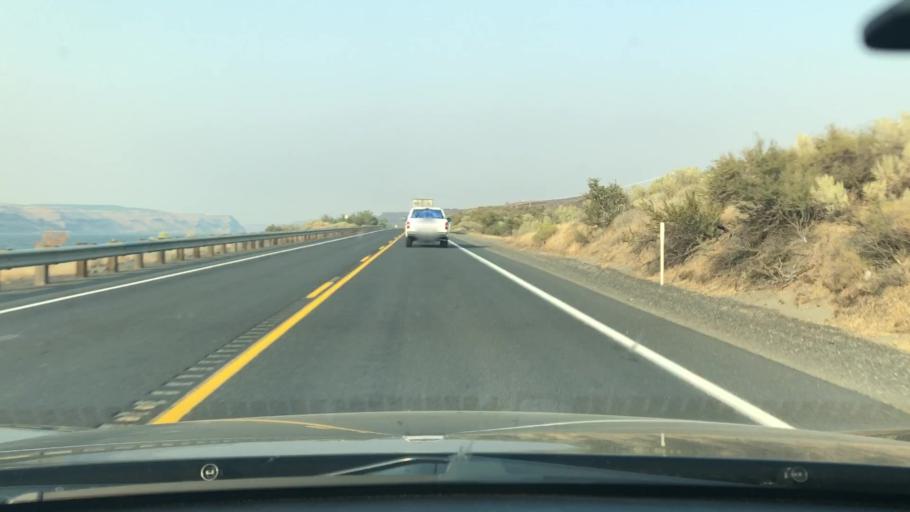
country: US
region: Oregon
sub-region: Umatilla County
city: Stanfield
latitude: 45.9255
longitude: -119.1076
